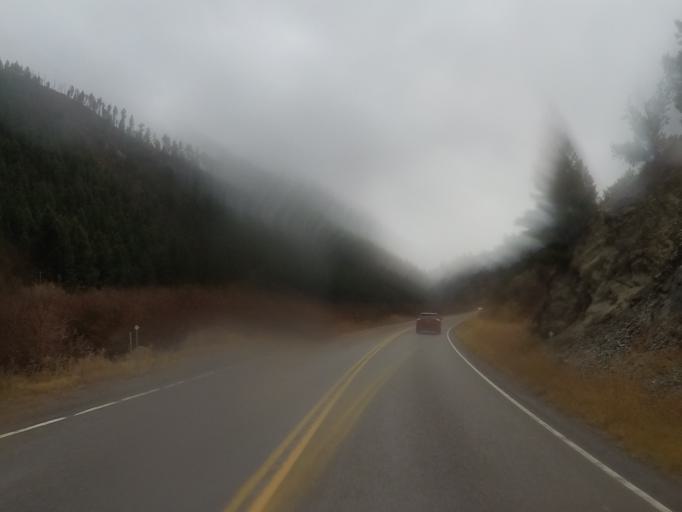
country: US
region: Montana
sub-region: Broadwater County
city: Townsend
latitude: 46.3340
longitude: -111.2265
